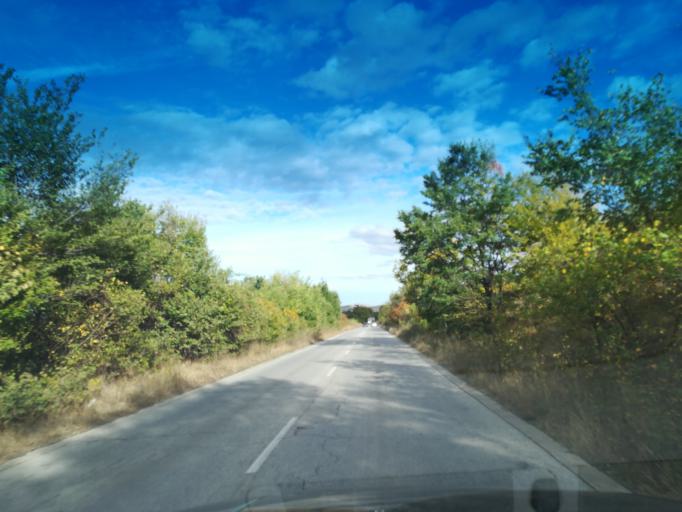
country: BG
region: Pazardzhik
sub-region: Obshtina Bratsigovo
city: Bratsigovo
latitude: 42.0685
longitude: 24.3920
